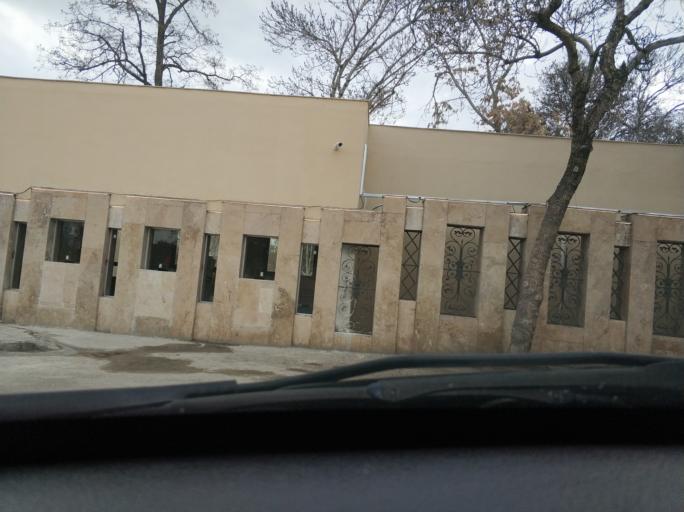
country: IR
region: Razavi Khorasan
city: Mashhad
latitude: 36.2551
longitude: 59.6109
